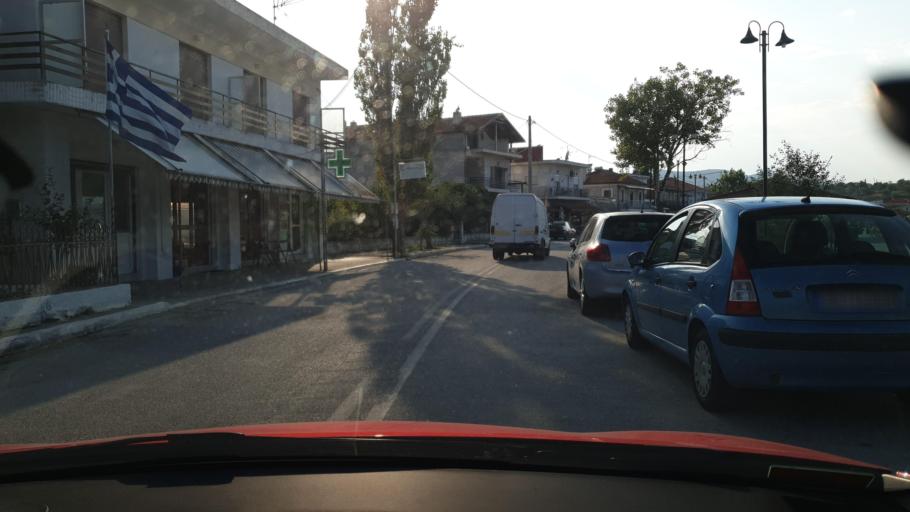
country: GR
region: Thessaly
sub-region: Nomos Magnisias
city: Pteleos
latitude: 39.0054
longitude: 22.9634
